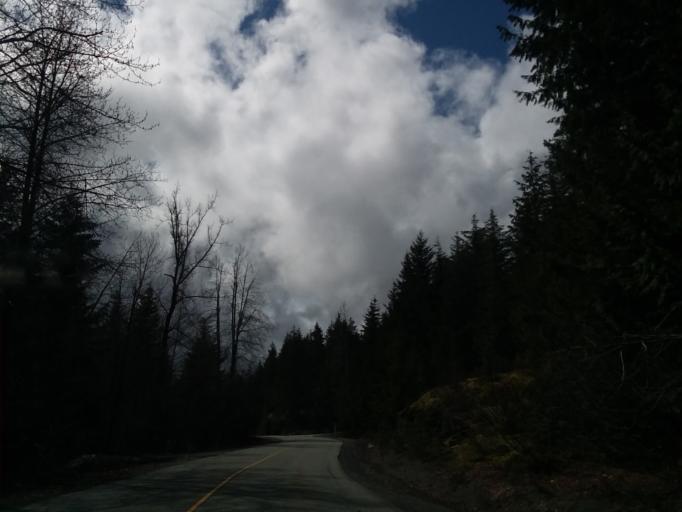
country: CA
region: British Columbia
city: Whistler
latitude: 50.1023
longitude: -123.0001
